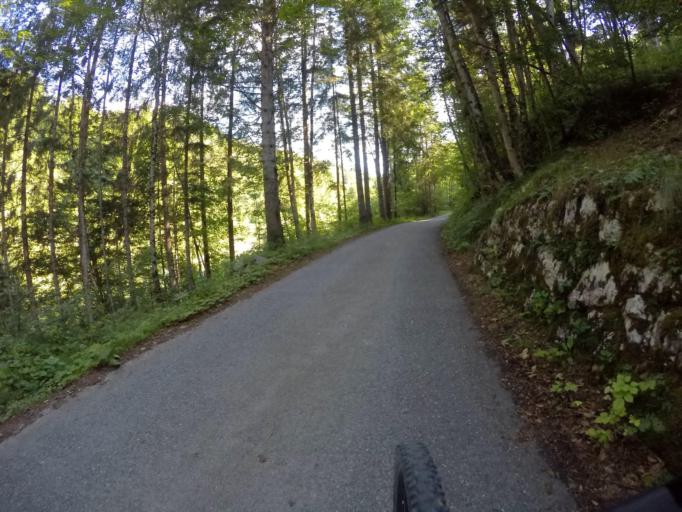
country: IT
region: Friuli Venezia Giulia
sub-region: Provincia di Udine
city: Zuglio
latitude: 46.4405
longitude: 13.0832
